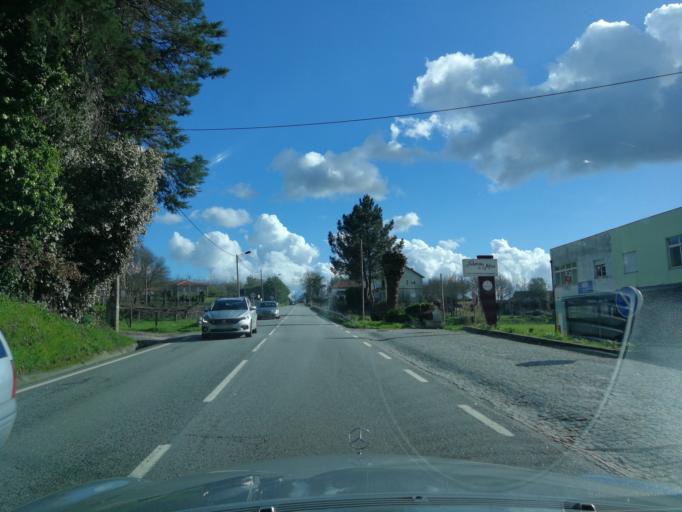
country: PT
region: Braga
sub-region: Vila Verde
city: Prado
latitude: 41.6714
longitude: -8.5236
